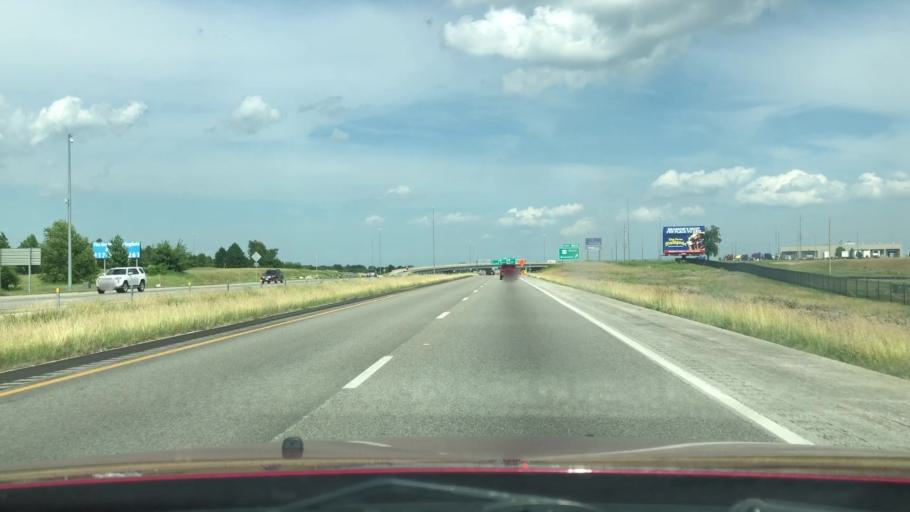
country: US
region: Missouri
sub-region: Greene County
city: Springfield
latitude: 37.2502
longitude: -93.2333
